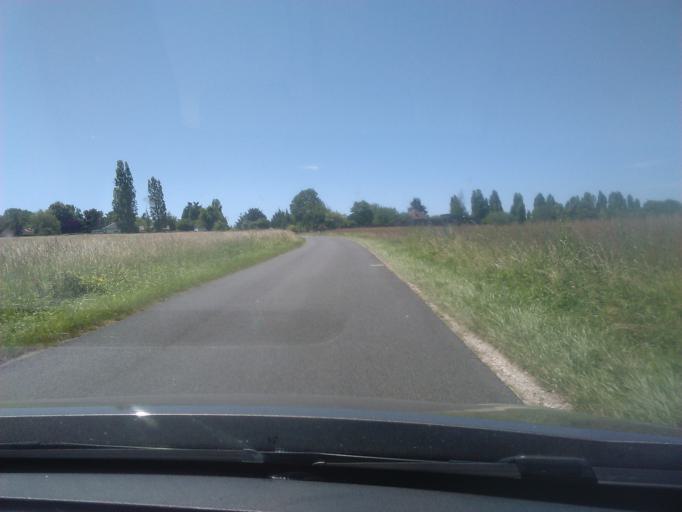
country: FR
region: Centre
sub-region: Departement du Loir-et-Cher
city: Saint-Sulpice-de-Pommeray
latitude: 47.6006
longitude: 1.2187
